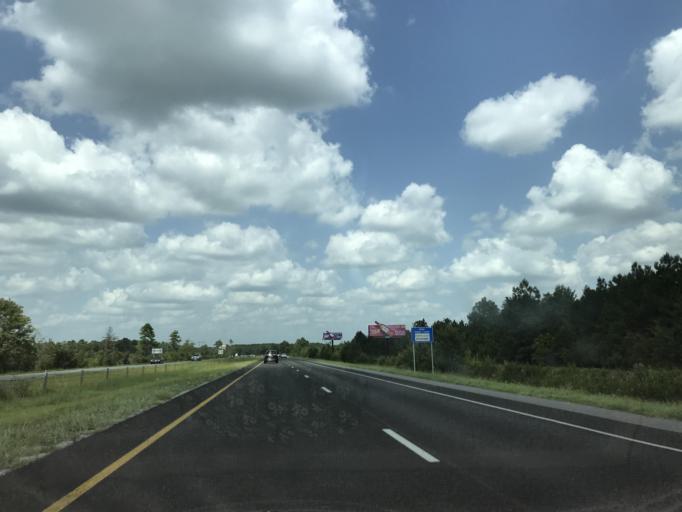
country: US
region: North Carolina
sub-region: Duplin County
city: Wallace
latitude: 34.7820
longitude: -77.9745
